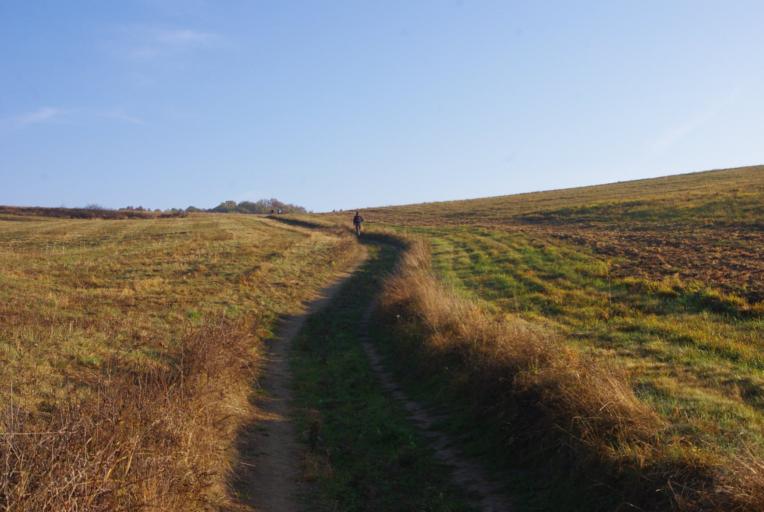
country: HU
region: Borsod-Abauj-Zemplen
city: Borsodnadasd
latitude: 48.0491
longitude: 20.2745
